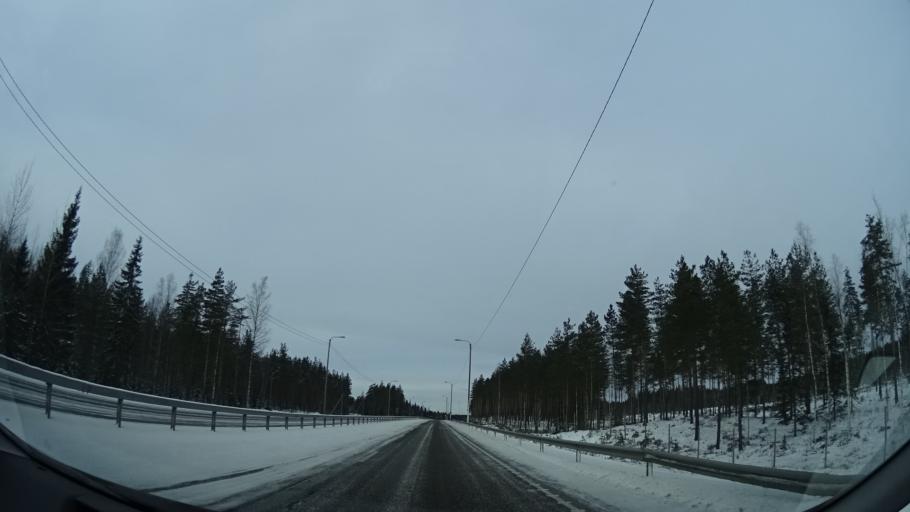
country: FI
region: Uusimaa
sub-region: Helsinki
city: Kaerkoelae
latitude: 60.6349
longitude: 23.9060
